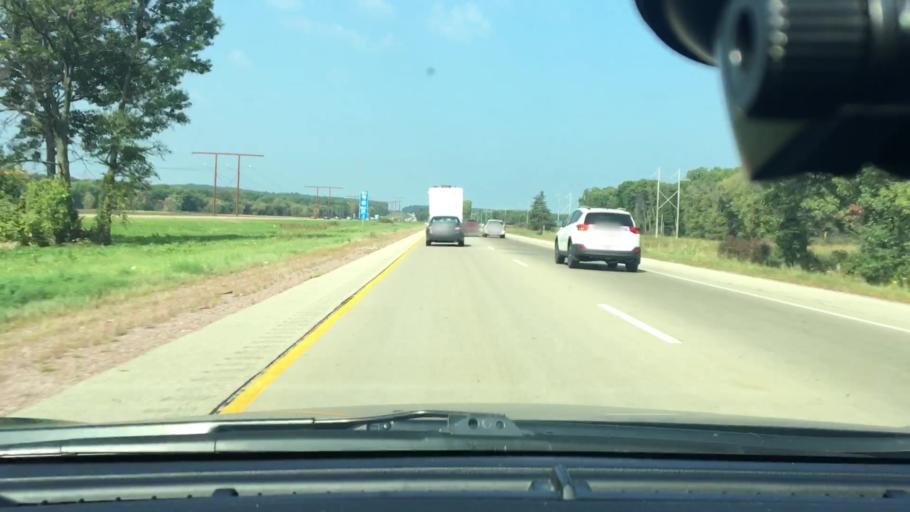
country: US
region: Wisconsin
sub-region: Columbia County
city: Portage
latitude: 43.5413
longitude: -89.6085
